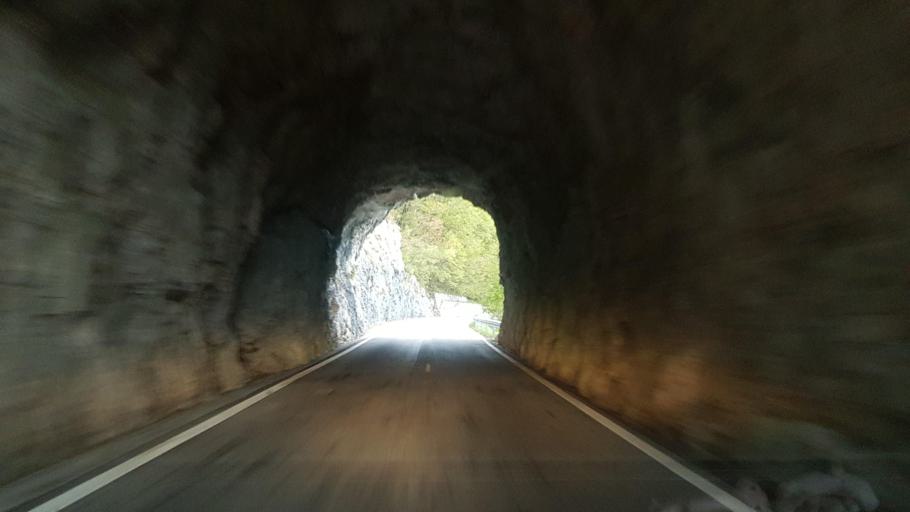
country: IT
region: Friuli Venezia Giulia
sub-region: Provincia di Udine
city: Villa Santina
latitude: 46.3475
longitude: 12.9176
